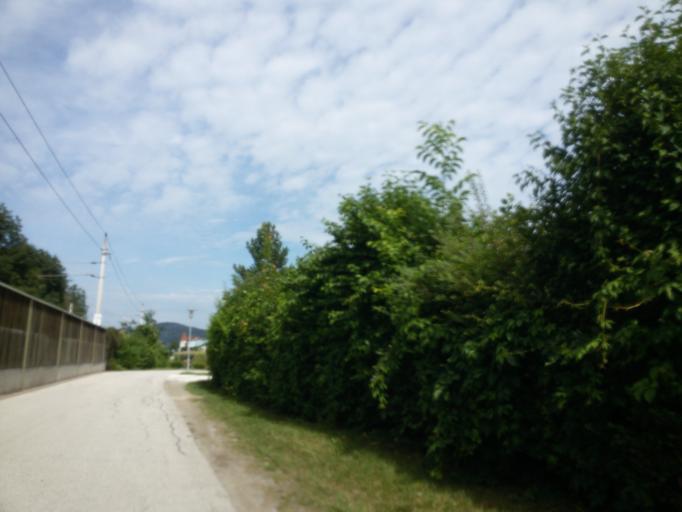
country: AT
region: Carinthia
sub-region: Politischer Bezirk Klagenfurt Land
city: Keutschach am See
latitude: 46.6210
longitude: 14.2012
